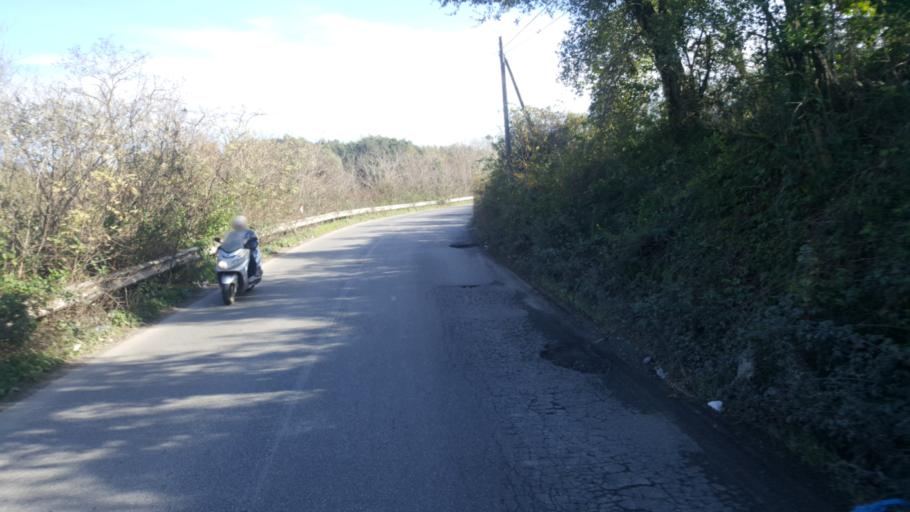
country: IT
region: Latium
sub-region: Citta metropolitana di Roma Capitale
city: Mantiglia di Ardea
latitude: 41.6880
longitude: 12.6049
